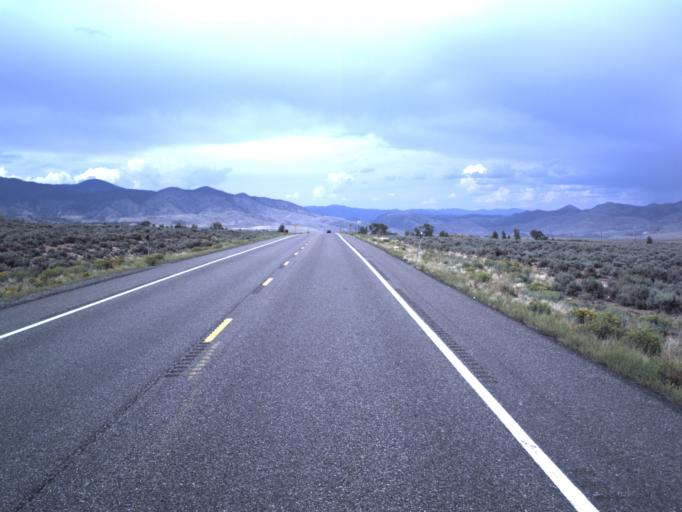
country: US
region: Utah
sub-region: Piute County
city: Junction
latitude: 38.3775
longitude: -112.2272
